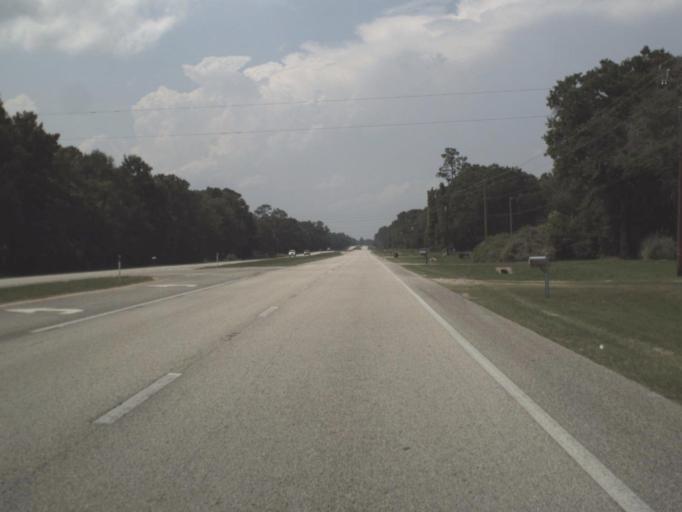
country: US
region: Florida
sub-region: Clay County
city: Green Cove Springs
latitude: 29.9111
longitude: -81.6783
